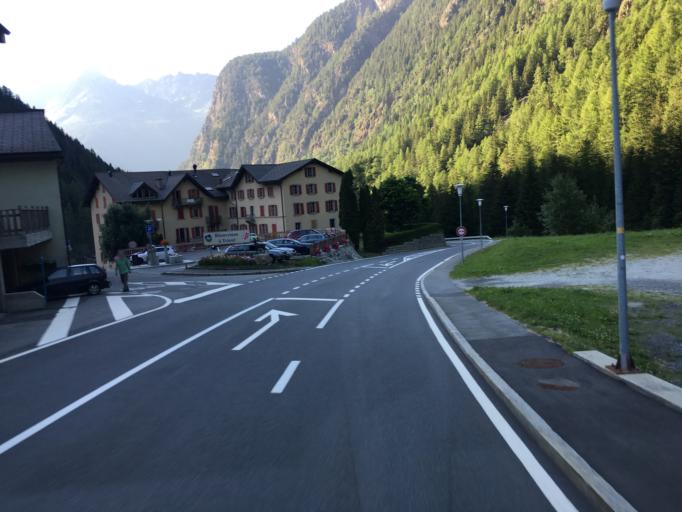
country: CH
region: Valais
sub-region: Martigny District
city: Martigny-Combe
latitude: 46.0555
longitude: 6.9963
